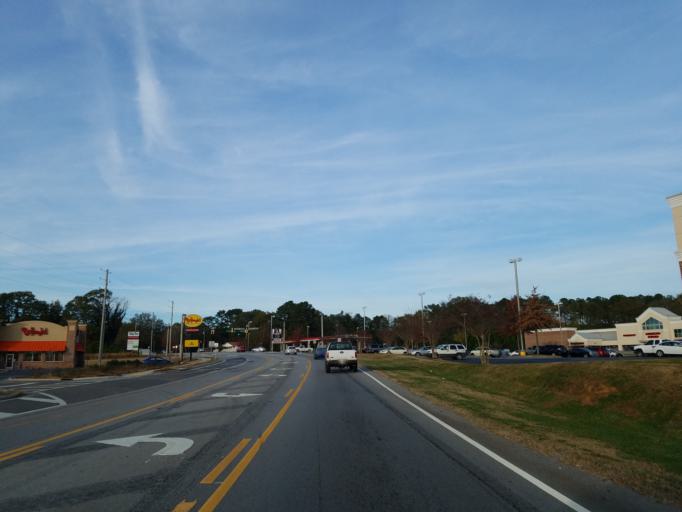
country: US
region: Georgia
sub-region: Carroll County
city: Temple
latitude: 33.7228
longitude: -85.0280
